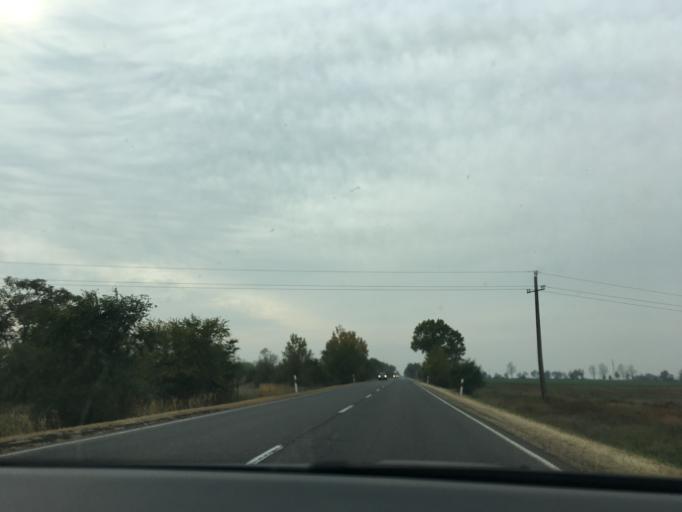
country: HU
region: Jasz-Nagykun-Szolnok
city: Karcag
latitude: 47.2844
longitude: 20.9044
